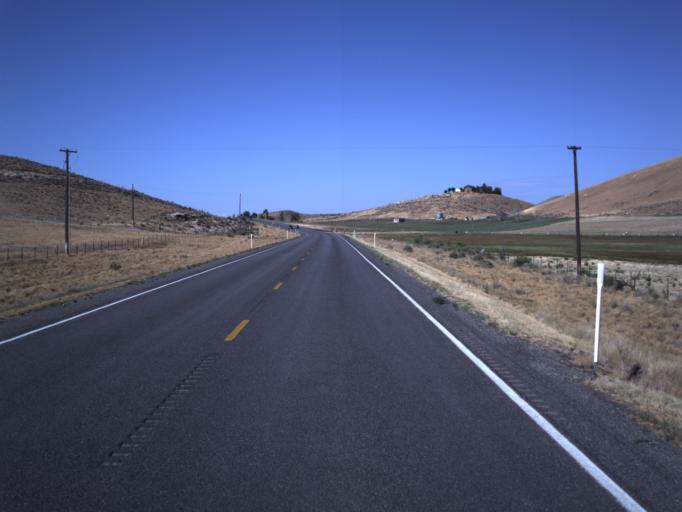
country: US
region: Utah
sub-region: Sanpete County
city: Manti
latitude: 39.2184
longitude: -111.6825
